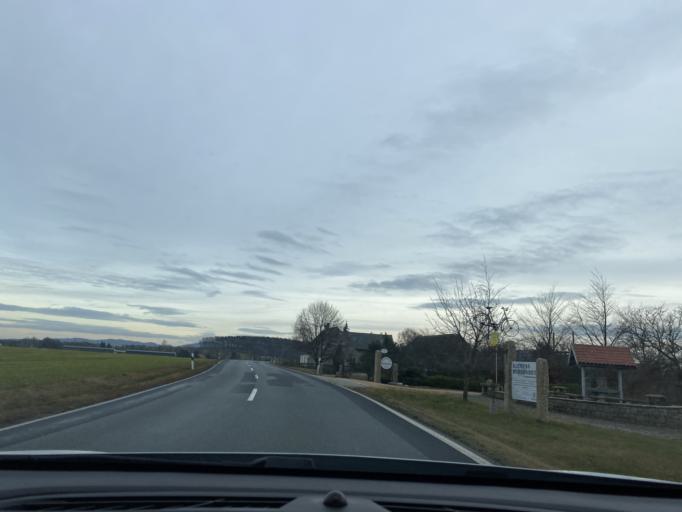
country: DE
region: Saxony
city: Reichenbach
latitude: 51.1199
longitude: 14.8279
